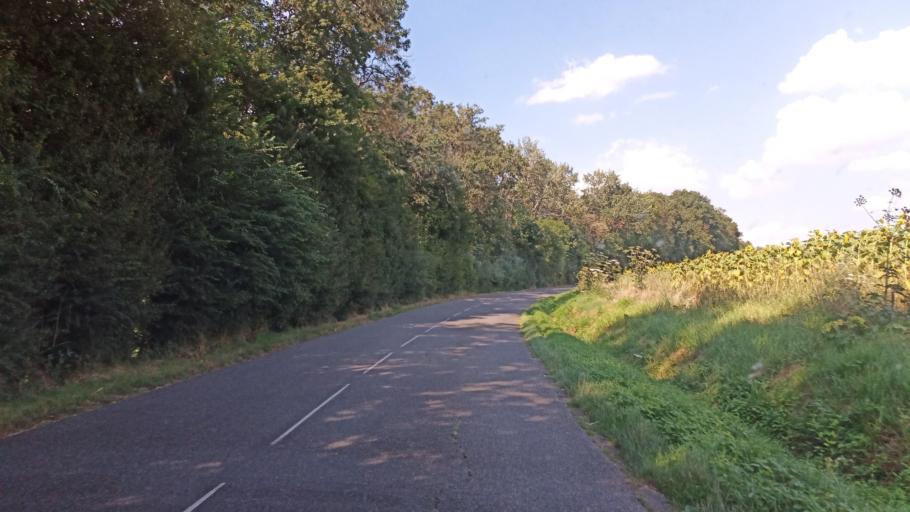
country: FR
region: Bourgogne
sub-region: Departement de l'Yonne
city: Saint-Valerien
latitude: 48.1535
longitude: 3.0913
